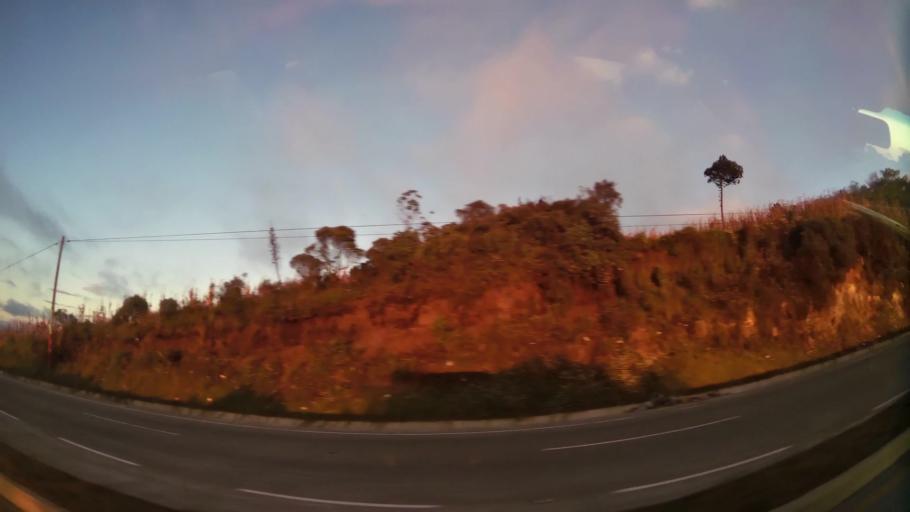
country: GT
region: Solola
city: Concepcion
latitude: 14.8347
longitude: -91.1146
